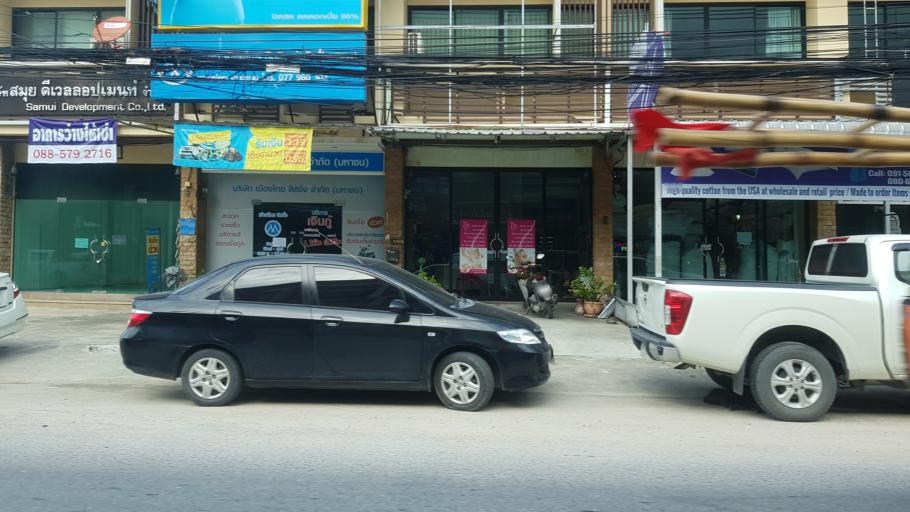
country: TH
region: Surat Thani
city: Ko Samui
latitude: 9.5355
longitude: 100.0417
